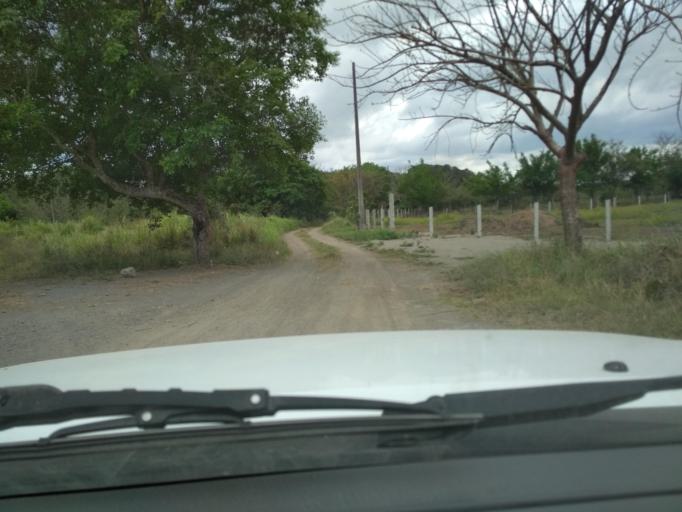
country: MX
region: Veracruz
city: El Tejar
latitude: 19.0597
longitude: -96.1479
